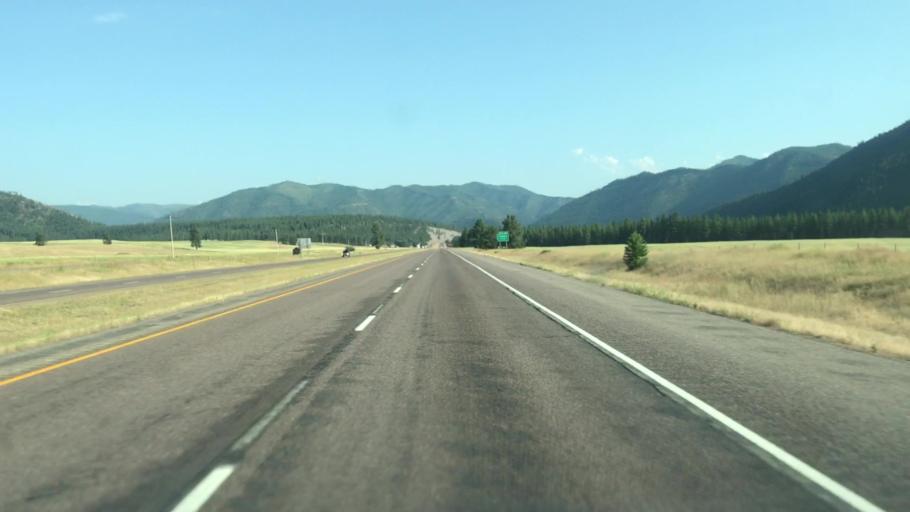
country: US
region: Montana
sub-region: Mineral County
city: Superior
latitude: 47.0438
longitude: -114.7514
